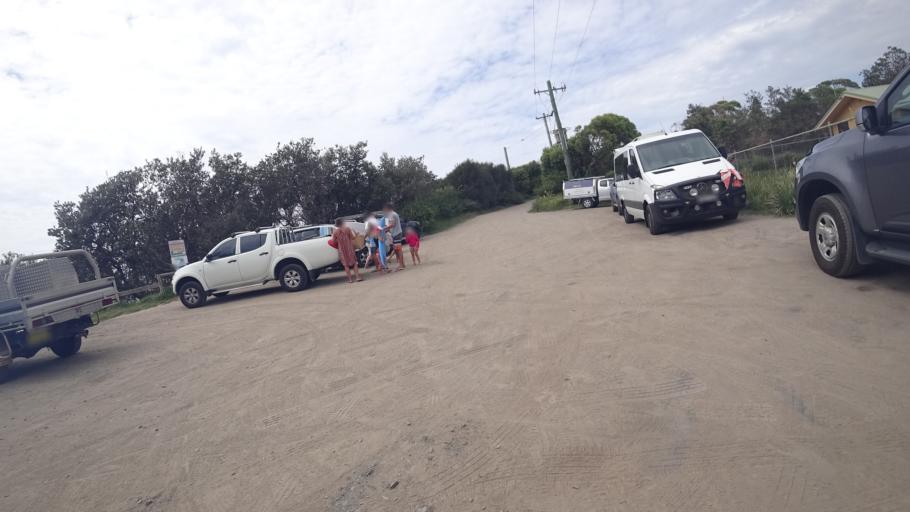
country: AU
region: New South Wales
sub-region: Shoalhaven Shire
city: Milton
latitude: -35.2549
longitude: 150.5262
